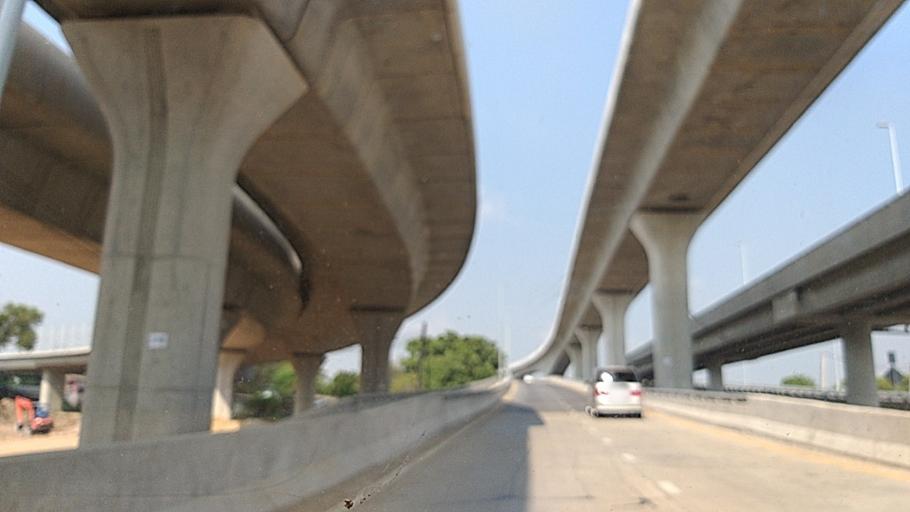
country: TH
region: Bangkok
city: Sai Mai
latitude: 13.9324
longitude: 100.6420
